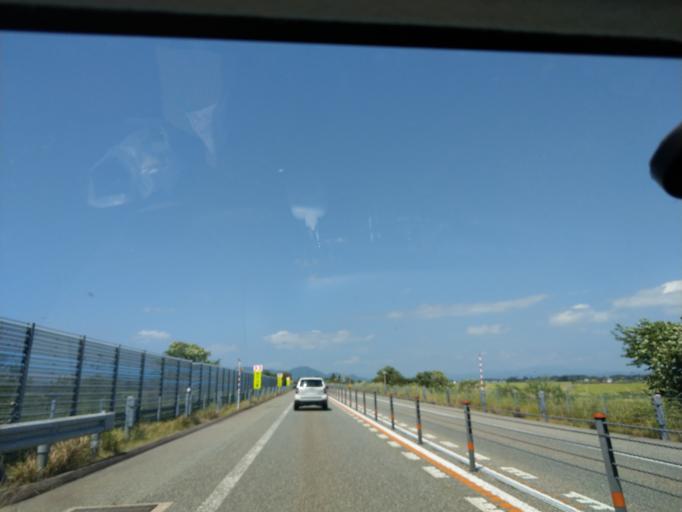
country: JP
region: Akita
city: Omagari
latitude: 39.3764
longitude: 140.4823
